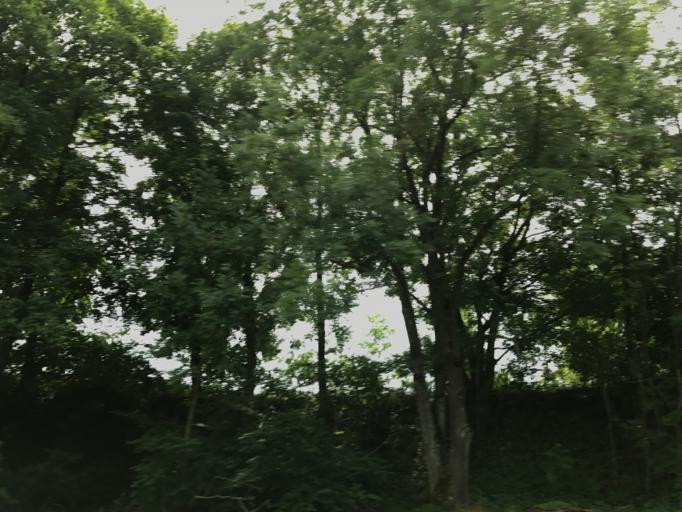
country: DE
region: Baden-Wuerttemberg
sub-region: Tuebingen Region
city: Boms
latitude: 47.9577
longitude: 9.5104
